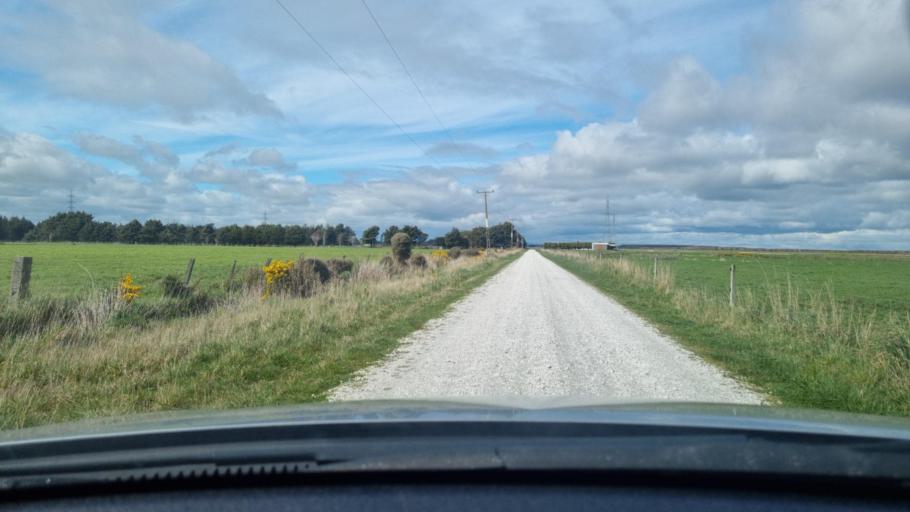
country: NZ
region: Southland
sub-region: Invercargill City
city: Invercargill
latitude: -46.4768
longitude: 168.4279
